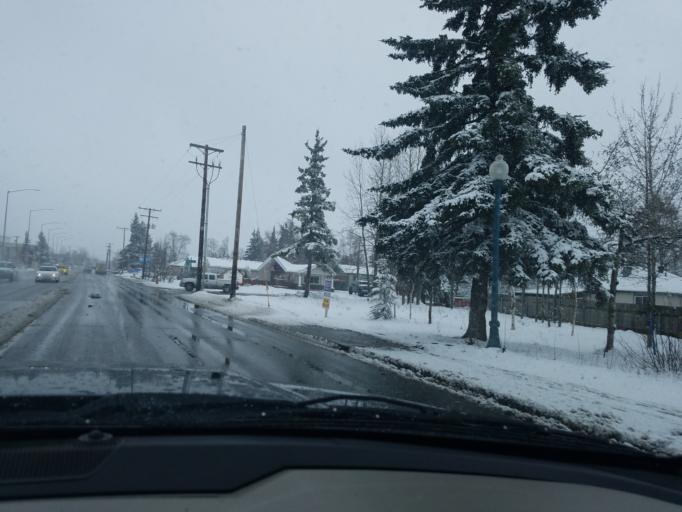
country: US
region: Alaska
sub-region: Anchorage Municipality
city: Anchorage
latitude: 61.1857
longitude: -149.9204
